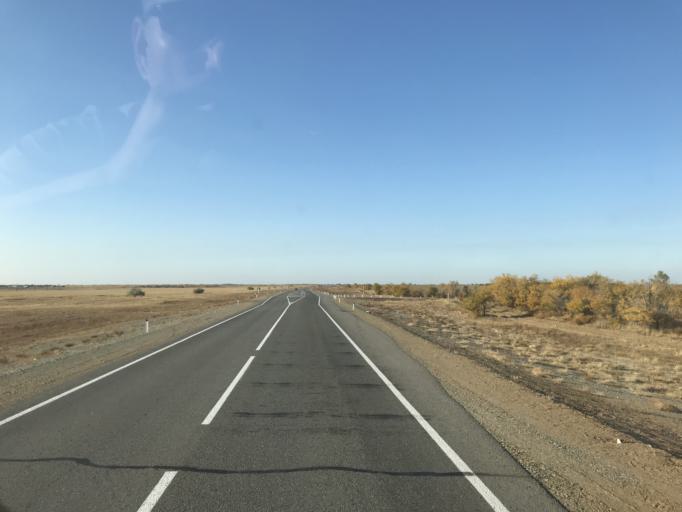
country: KZ
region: Pavlodar
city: Koktobe
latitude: 51.7991
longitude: 77.4828
